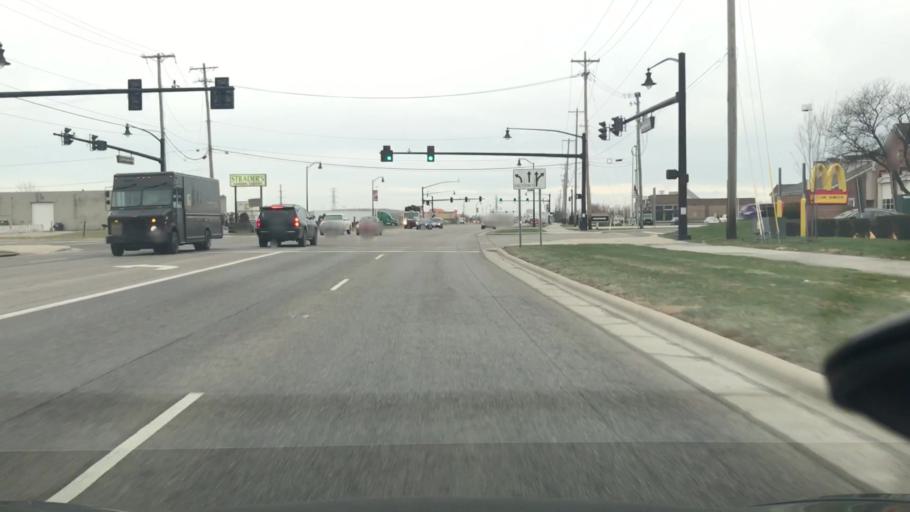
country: US
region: Ohio
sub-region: Franklin County
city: Grove City
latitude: 39.8392
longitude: -83.0754
